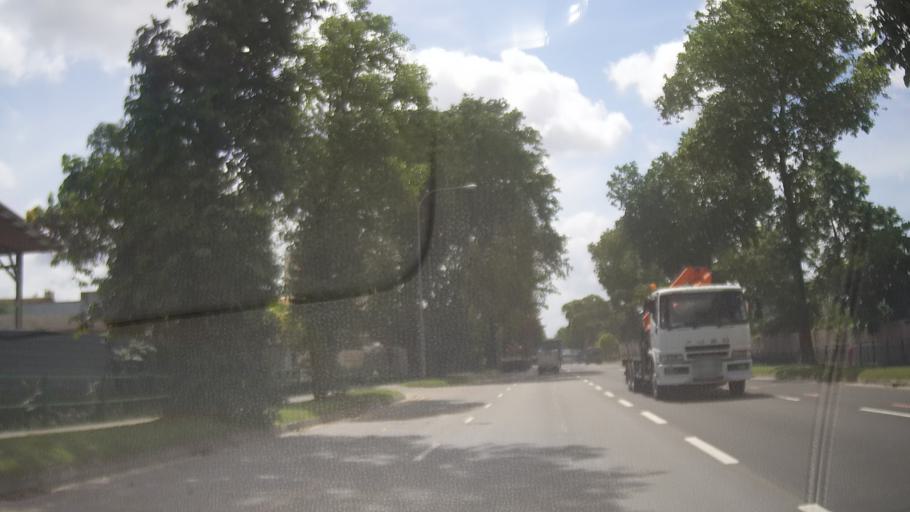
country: MY
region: Johor
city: Johor Bahru
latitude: 1.4248
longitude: 103.7498
